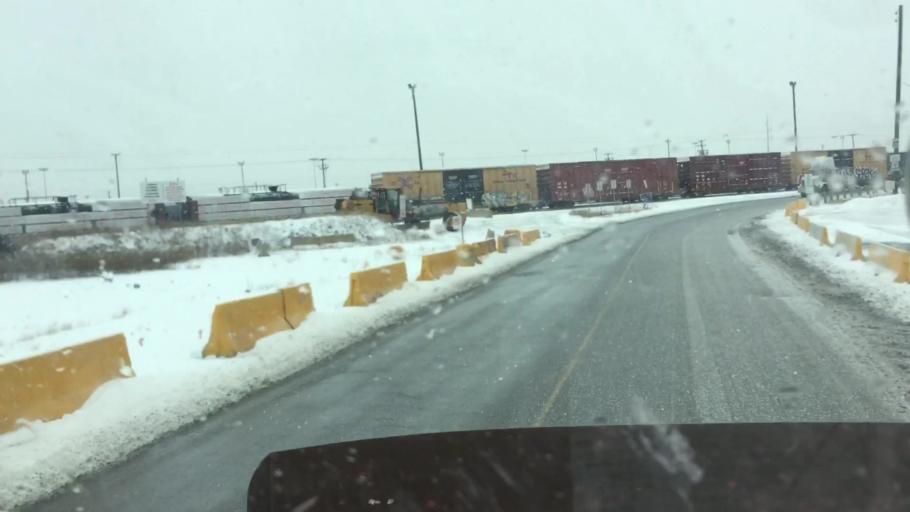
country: CA
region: Quebec
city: Cote-Saint-Luc
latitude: 45.4724
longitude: -73.6933
